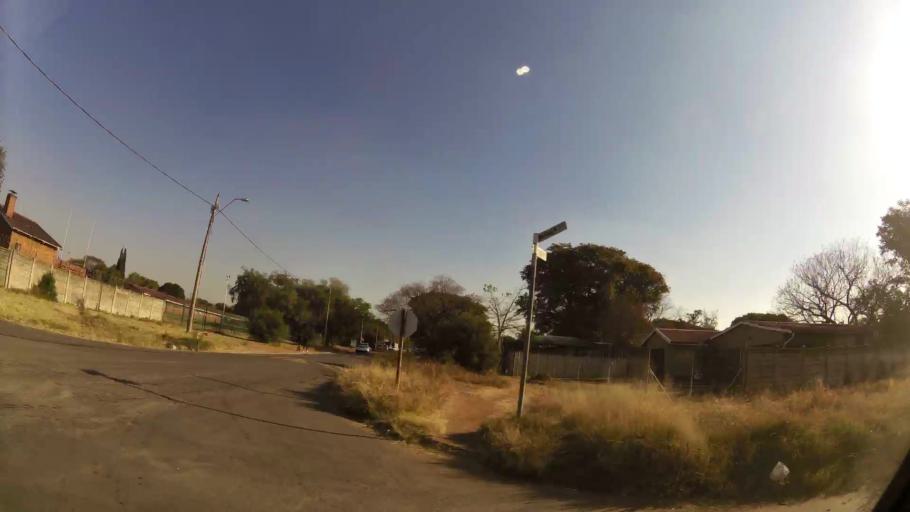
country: ZA
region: North-West
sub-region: Bojanala Platinum District Municipality
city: Rustenburg
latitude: -25.6564
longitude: 27.2571
